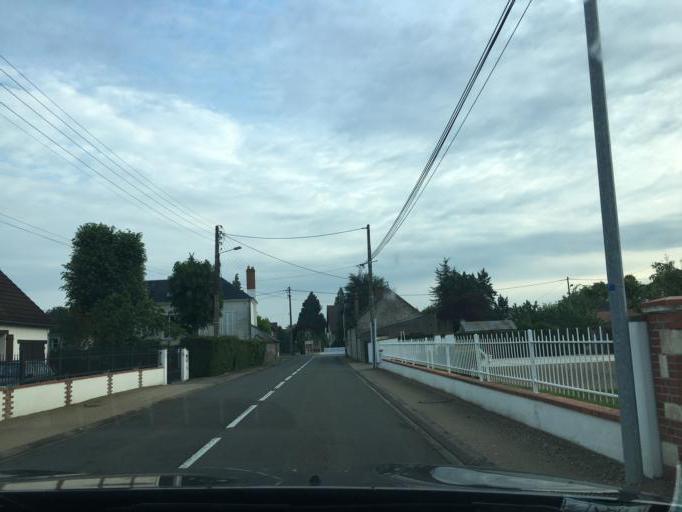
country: FR
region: Centre
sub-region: Departement du Loiret
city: Saint-Denis-en-Val
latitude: 47.8789
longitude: 1.9511
